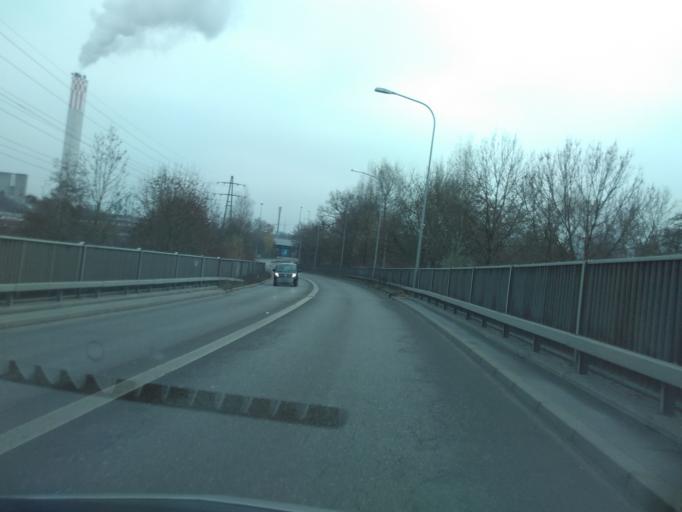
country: CH
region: Zurich
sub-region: Bezirk Zuerich
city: Zuerich (Kreis 12) / Saatlen
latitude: 47.4124
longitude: 8.5680
